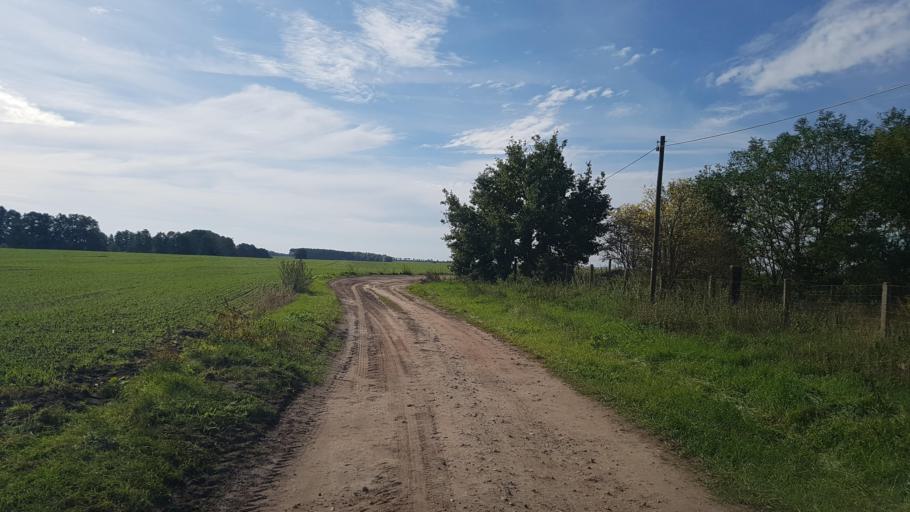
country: DE
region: Brandenburg
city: Juterbog
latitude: 51.9800
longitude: 13.0926
